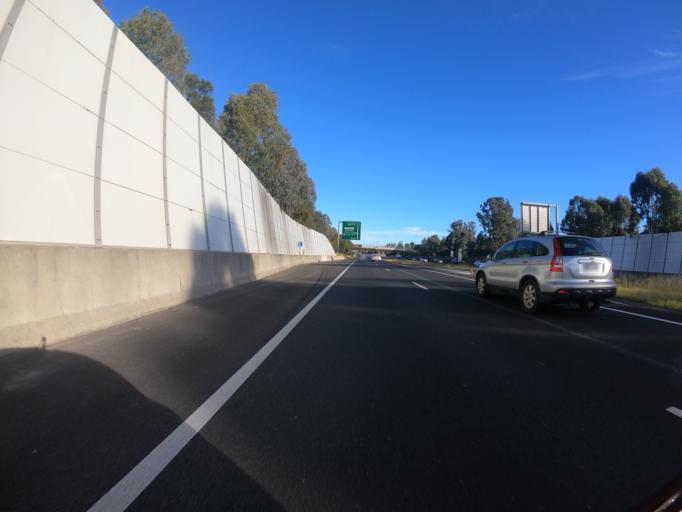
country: AU
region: New South Wales
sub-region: Blacktown
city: Glendenning
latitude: -33.7429
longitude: 150.8473
